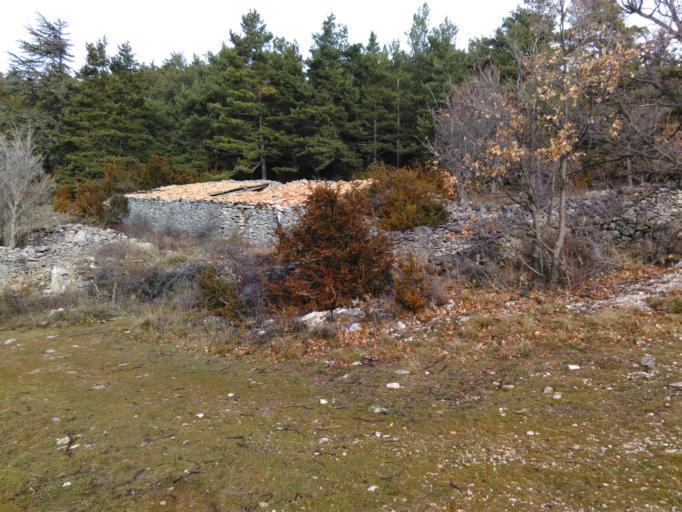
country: FR
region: Provence-Alpes-Cote d'Azur
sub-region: Departement du Vaucluse
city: Bedoin
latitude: 44.1520
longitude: 5.2423
